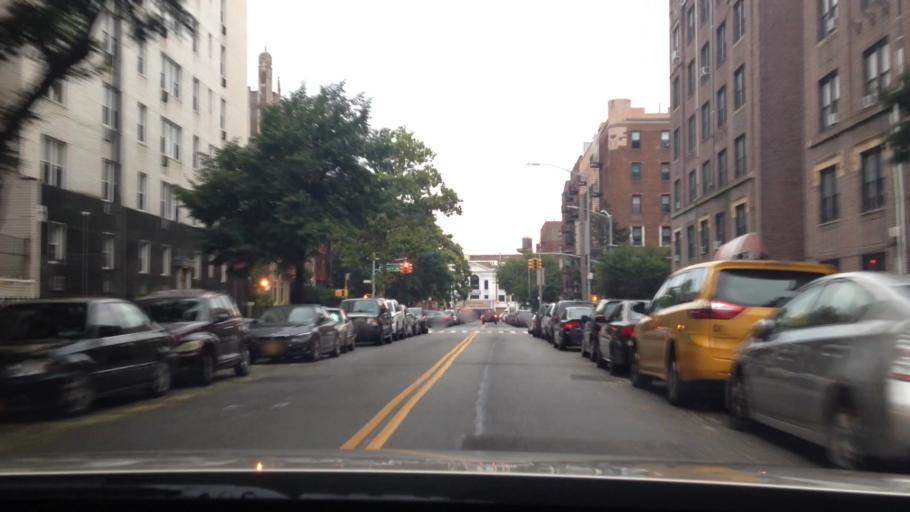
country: US
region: New York
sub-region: Kings County
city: Brooklyn
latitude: 40.6471
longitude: -73.9614
